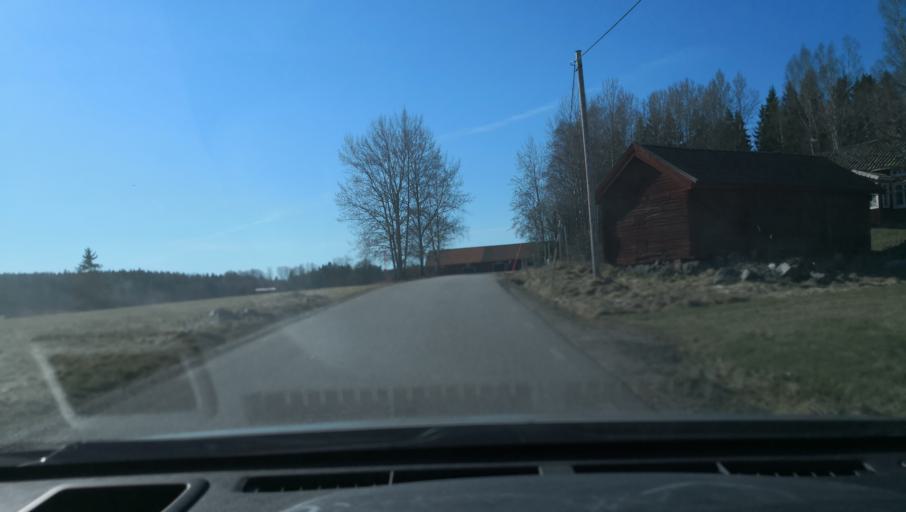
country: SE
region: Vaestmanland
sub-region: Sala Kommun
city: Sala
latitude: 60.0802
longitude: 16.4596
